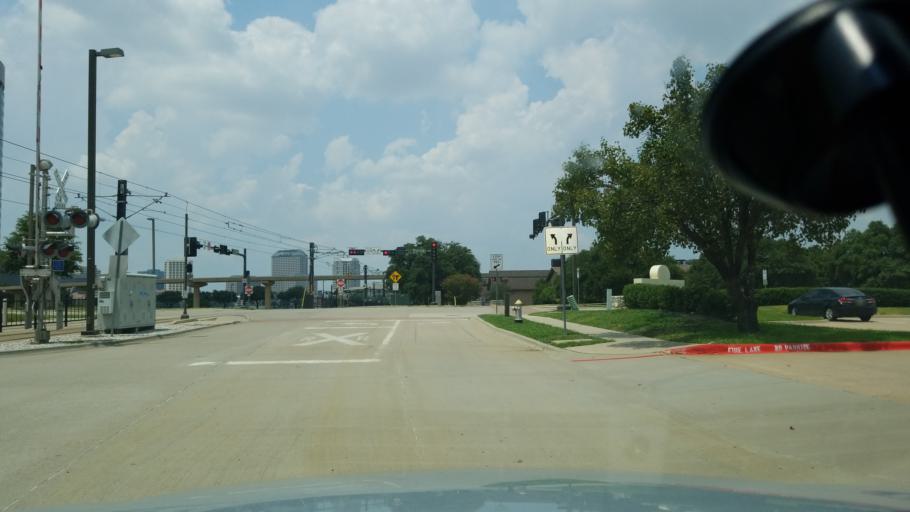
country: US
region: Texas
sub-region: Dallas County
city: Irving
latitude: 32.8594
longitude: -96.9270
